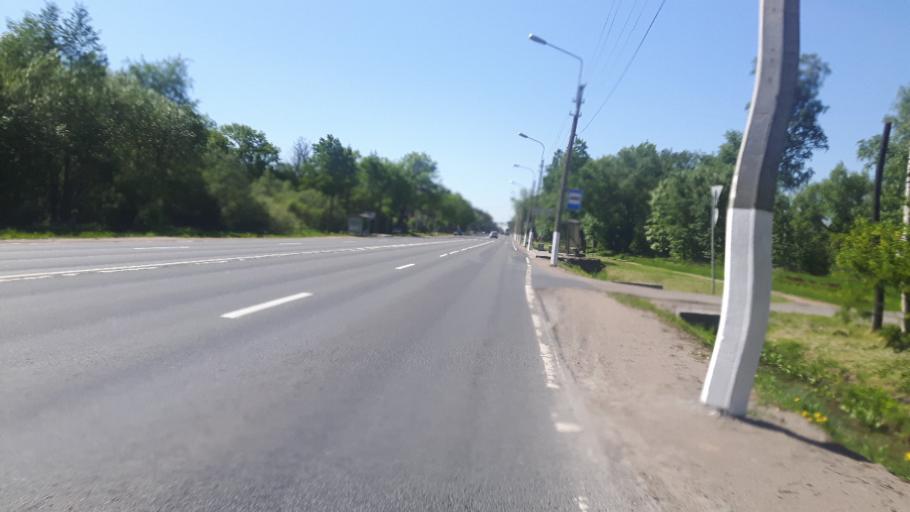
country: RU
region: Leningrad
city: Ol'gino
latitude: 59.8737
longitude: 29.9537
